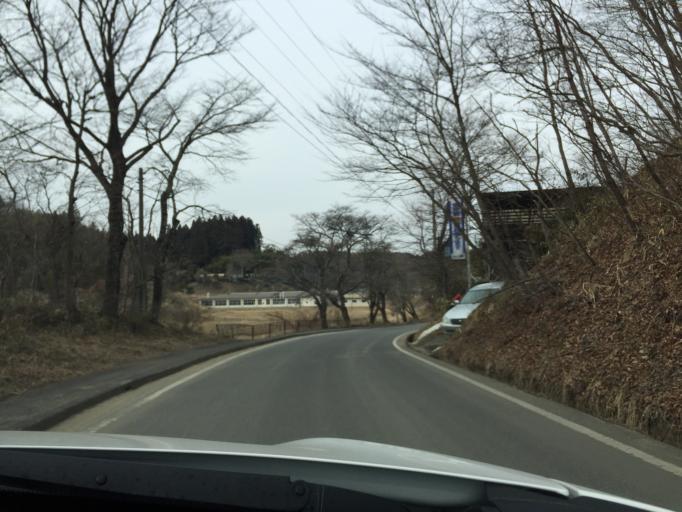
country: JP
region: Fukushima
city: Ishikawa
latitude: 37.1796
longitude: 140.5682
